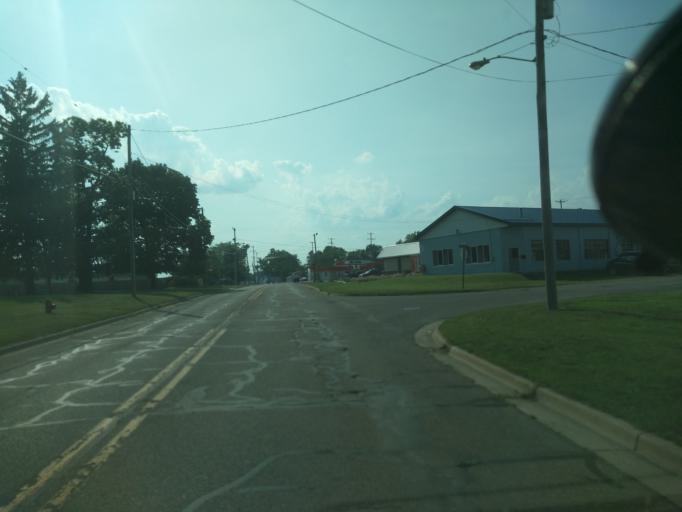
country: US
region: Michigan
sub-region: Jackson County
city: Jackson
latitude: 42.2538
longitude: -84.4357
